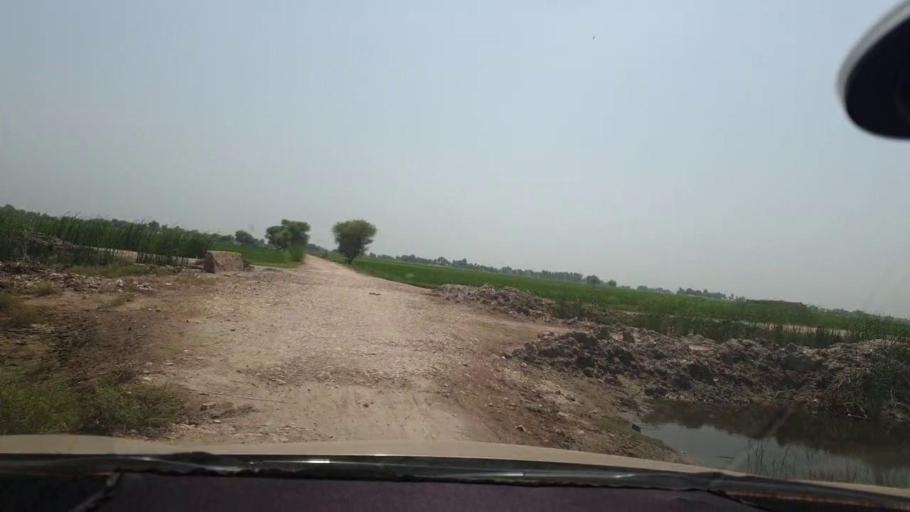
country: PK
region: Sindh
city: Kambar
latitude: 27.6462
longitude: 67.9320
